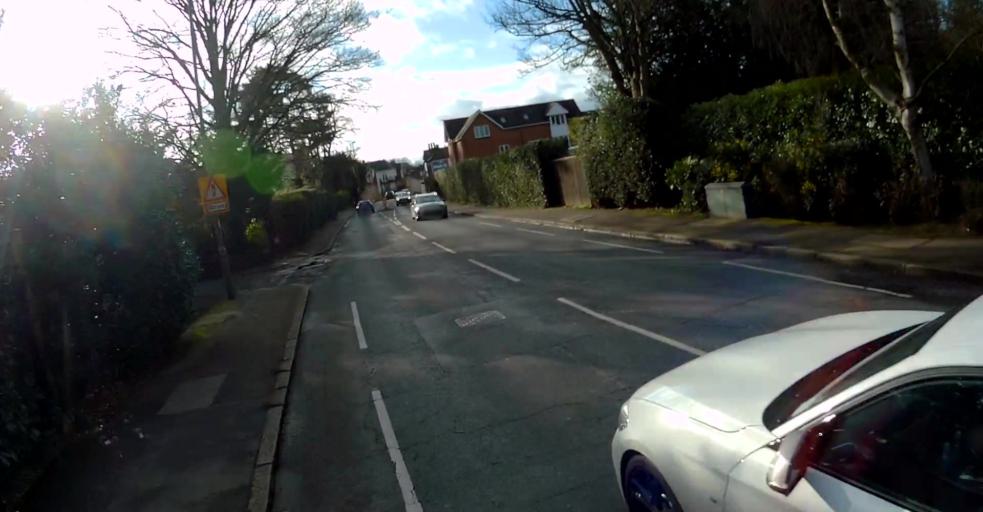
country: GB
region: England
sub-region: Surrey
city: Weybridge
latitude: 51.3747
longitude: -0.4375
